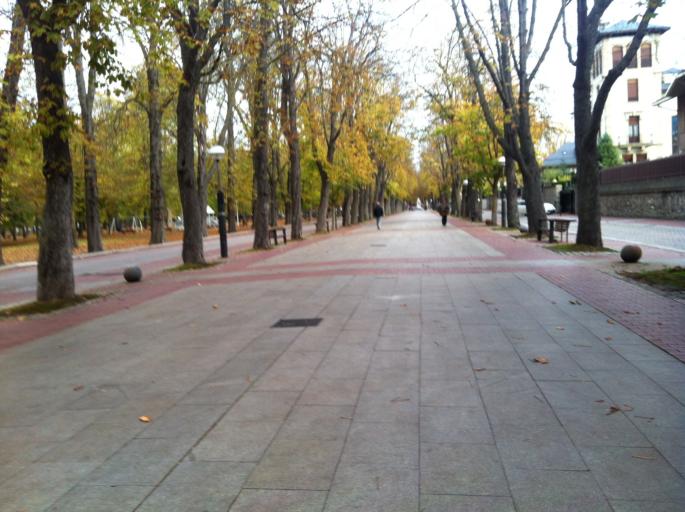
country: ES
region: Basque Country
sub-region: Provincia de Alava
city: Gasteiz / Vitoria
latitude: 42.8403
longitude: -2.6863
